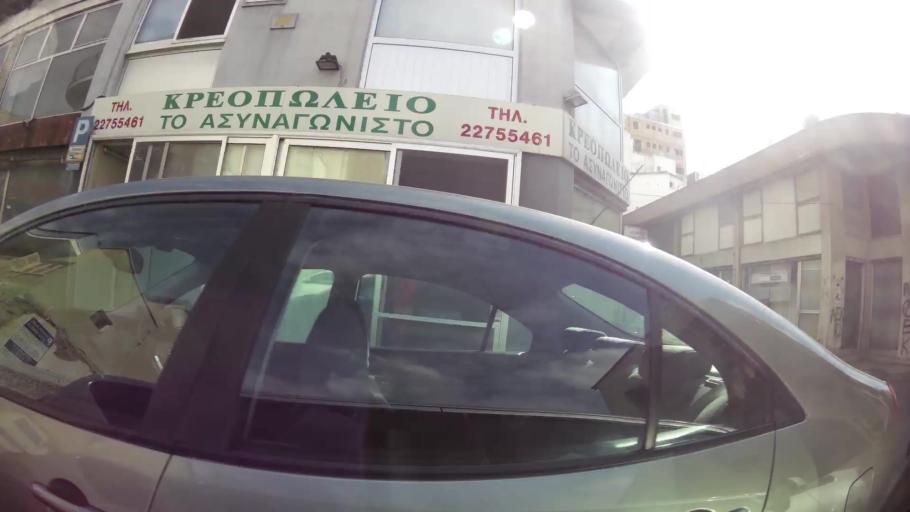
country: CY
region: Lefkosia
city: Nicosia
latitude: 35.1702
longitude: 33.3639
